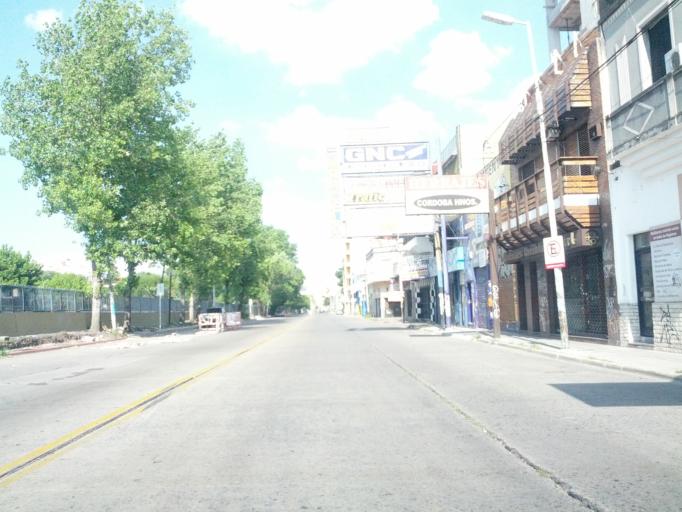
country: AR
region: Buenos Aires
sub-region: Partido de Moron
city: Moron
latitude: -34.6438
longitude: -58.5841
